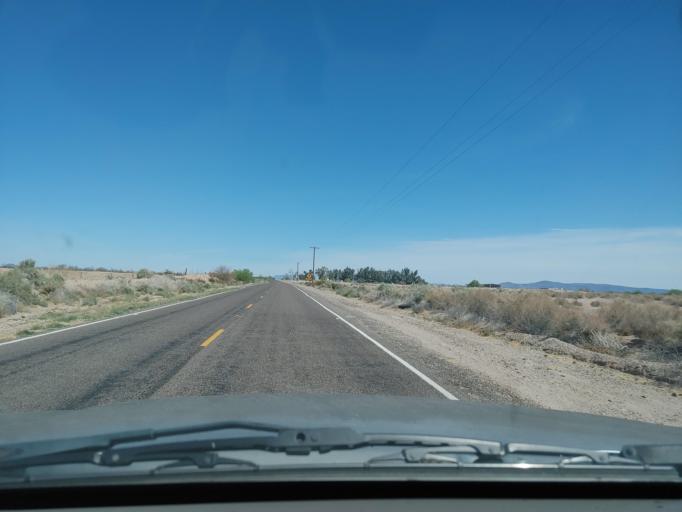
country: US
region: Arizona
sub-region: Maricopa County
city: Gila Bend
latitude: 32.9837
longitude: -113.3059
